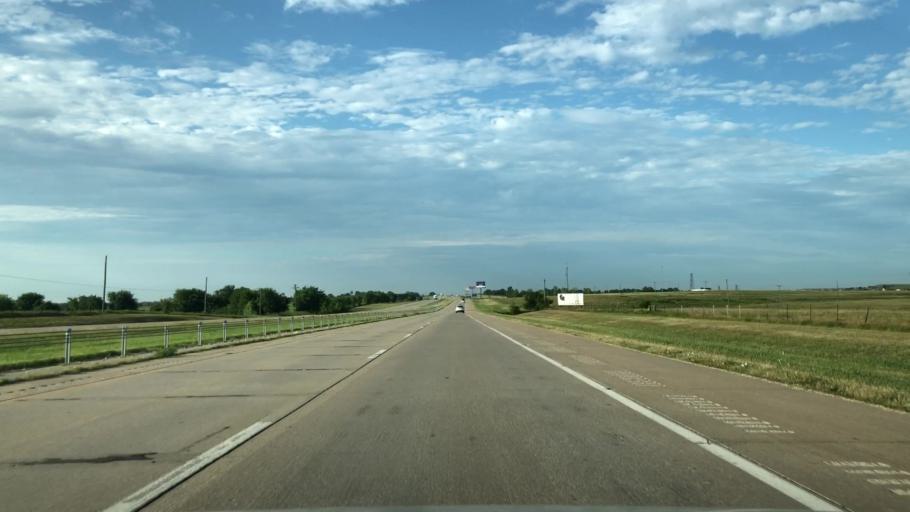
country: US
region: Oklahoma
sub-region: Osage County
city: Skiatook
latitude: 36.3798
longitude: -95.9207
